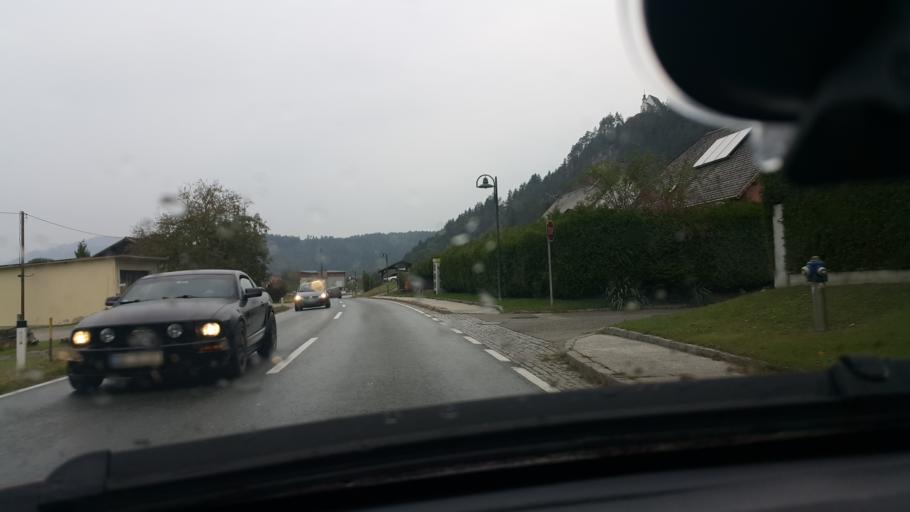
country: AT
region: Carinthia
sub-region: Politischer Bezirk Wolfsberg
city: Lavamund
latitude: 46.6374
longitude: 14.9542
